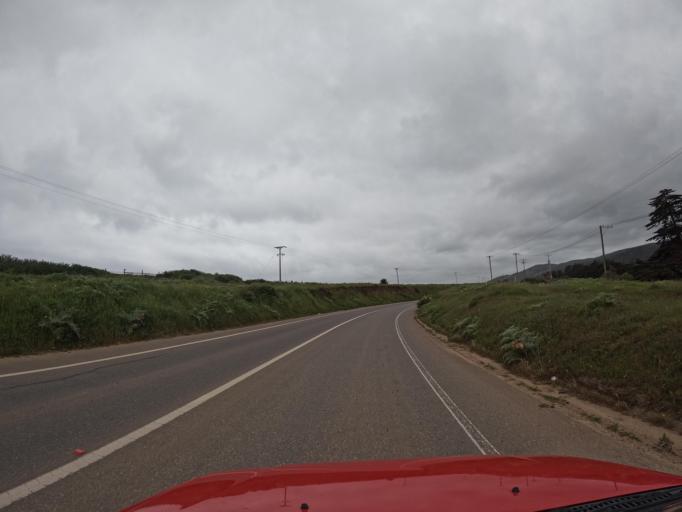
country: CL
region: O'Higgins
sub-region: Provincia de Colchagua
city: Santa Cruz
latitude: -34.4884
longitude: -72.0197
